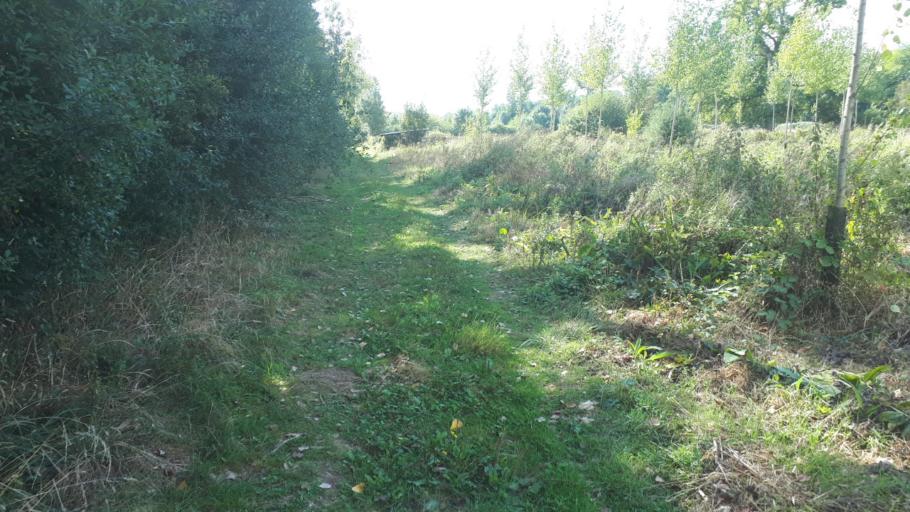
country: FR
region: Centre
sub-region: Departement du Loir-et-Cher
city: Villiers-sur-Loir
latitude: 47.8205
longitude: 0.9674
